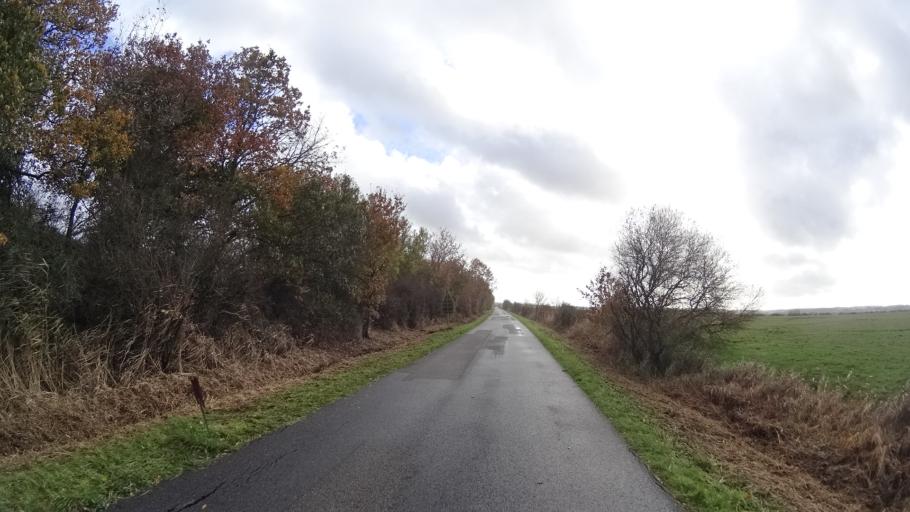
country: FR
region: Brittany
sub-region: Departement du Morbihan
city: Rieux
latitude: 47.5965
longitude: -2.0904
